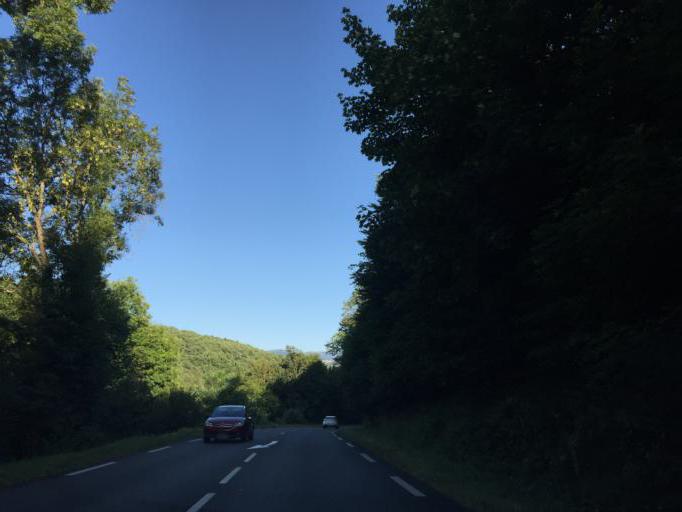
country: FR
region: Rhone-Alpes
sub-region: Departement de la Loire
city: Sorbiers
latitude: 45.4808
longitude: 4.4620
